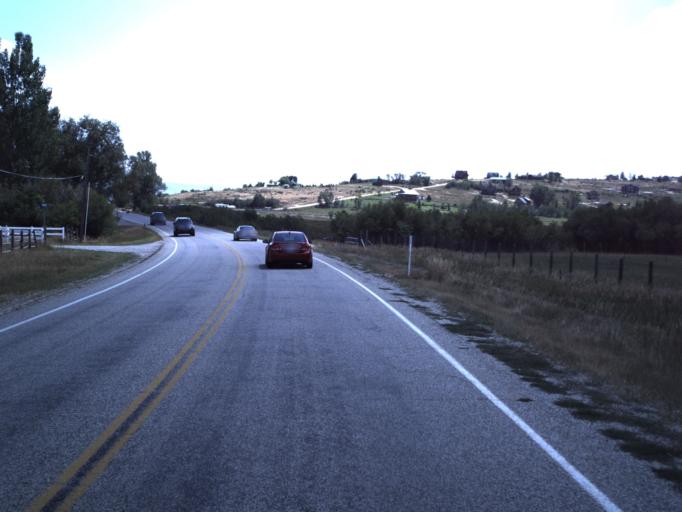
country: US
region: Idaho
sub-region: Bear Lake County
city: Paris
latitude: 41.9836
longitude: -111.4099
